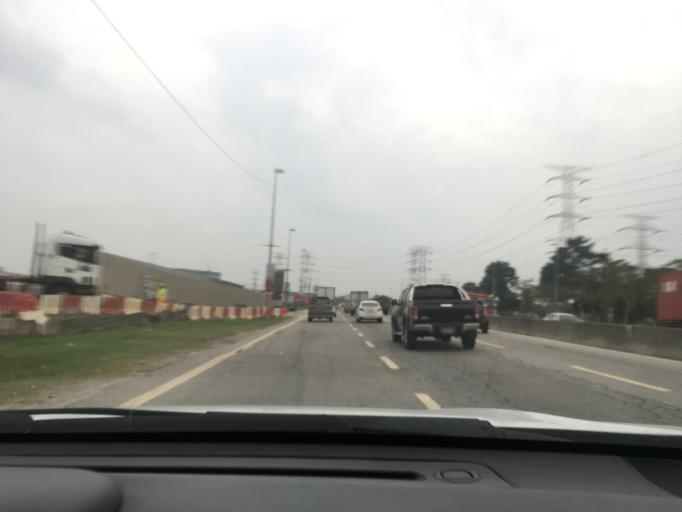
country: MY
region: Selangor
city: Klang
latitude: 3.0993
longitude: 101.4427
